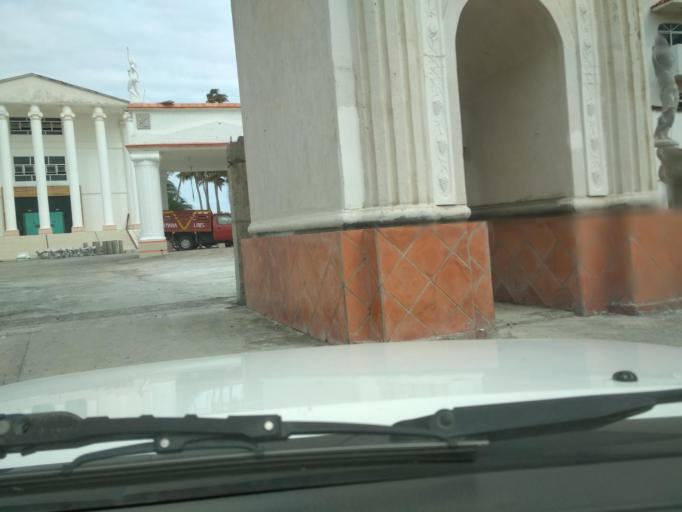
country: MX
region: Veracruz
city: Anton Lizardo
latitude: 19.0392
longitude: -95.9702
